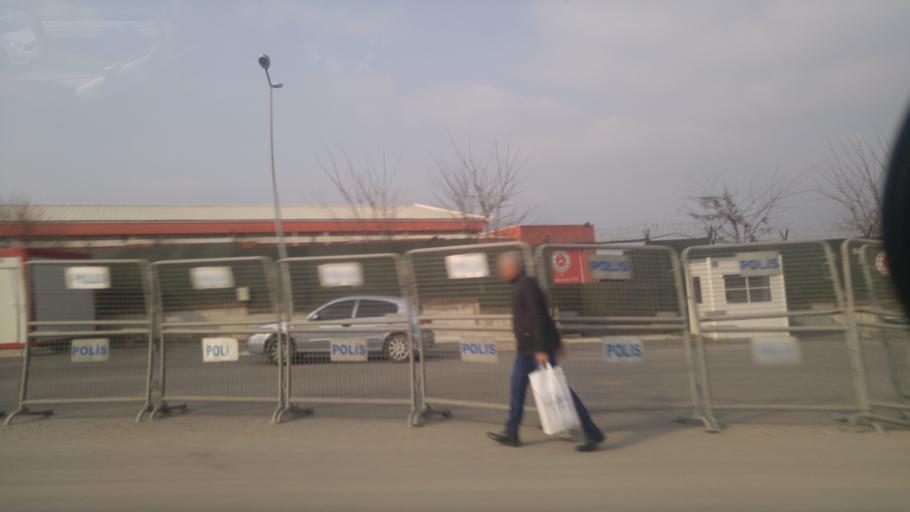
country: TR
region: Istanbul
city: Mimarsinan
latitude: 41.0156
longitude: 28.5519
